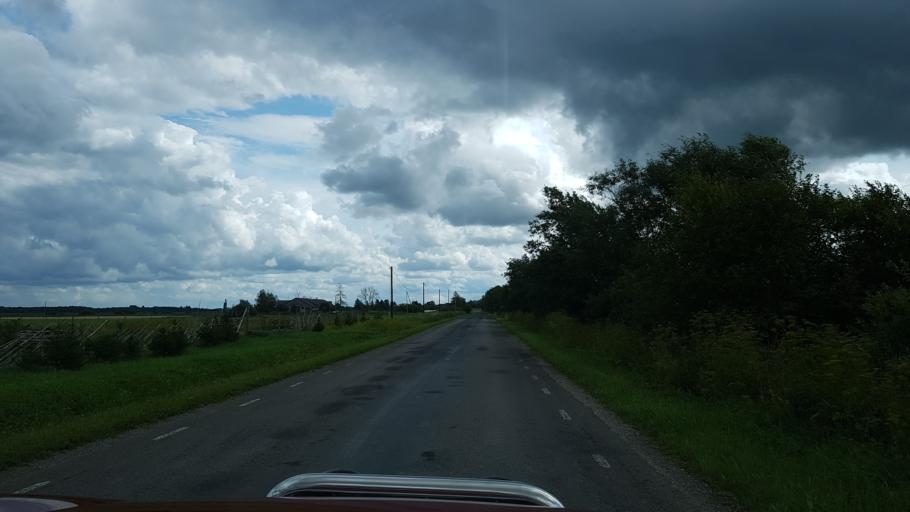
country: EE
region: Laeaene
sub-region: Lihula vald
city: Lihula
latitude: 58.7185
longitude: 23.9838
